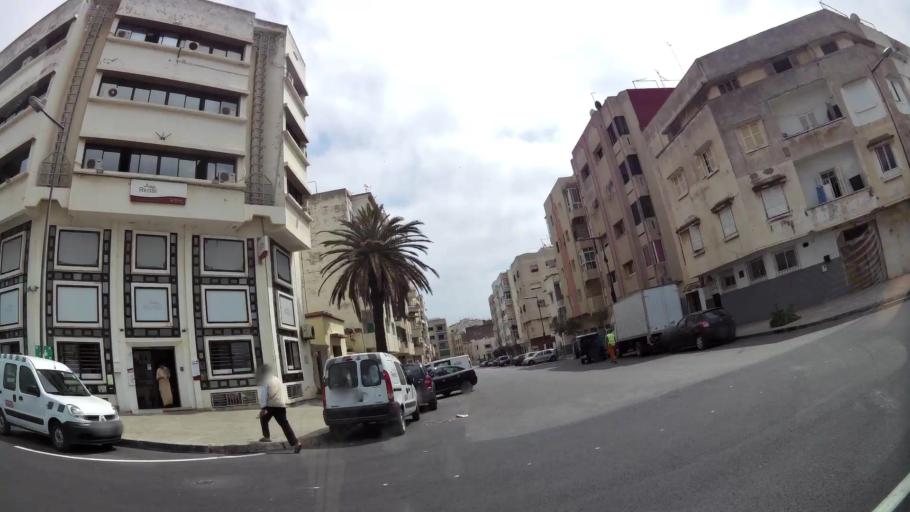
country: MA
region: Rabat-Sale-Zemmour-Zaer
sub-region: Rabat
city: Rabat
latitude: 34.0200
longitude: -6.8526
